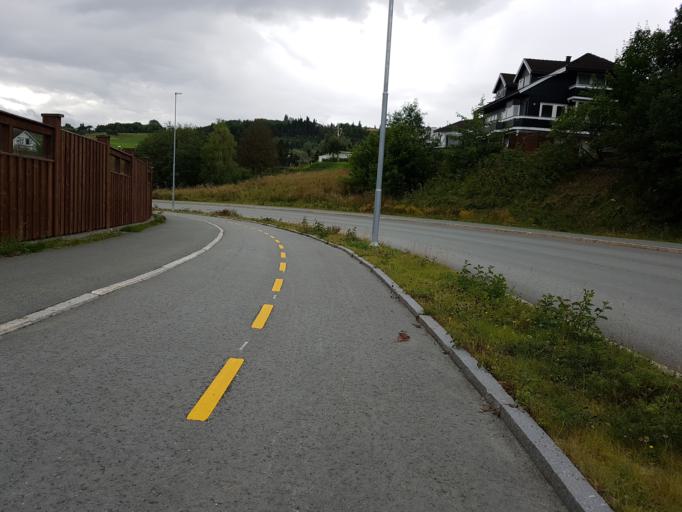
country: NO
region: Sor-Trondelag
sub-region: Trondheim
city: Trondheim
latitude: 63.3878
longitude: 10.3475
